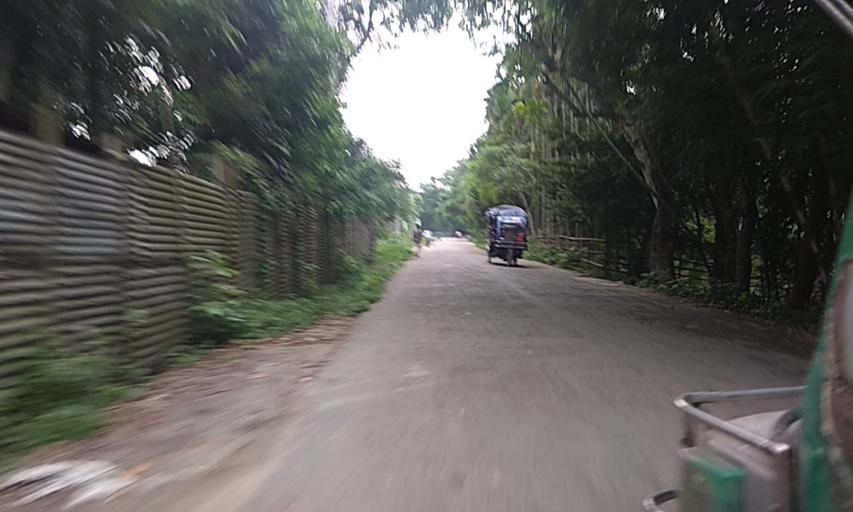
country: BD
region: Dhaka
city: Dohar
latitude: 23.4563
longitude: 90.0148
